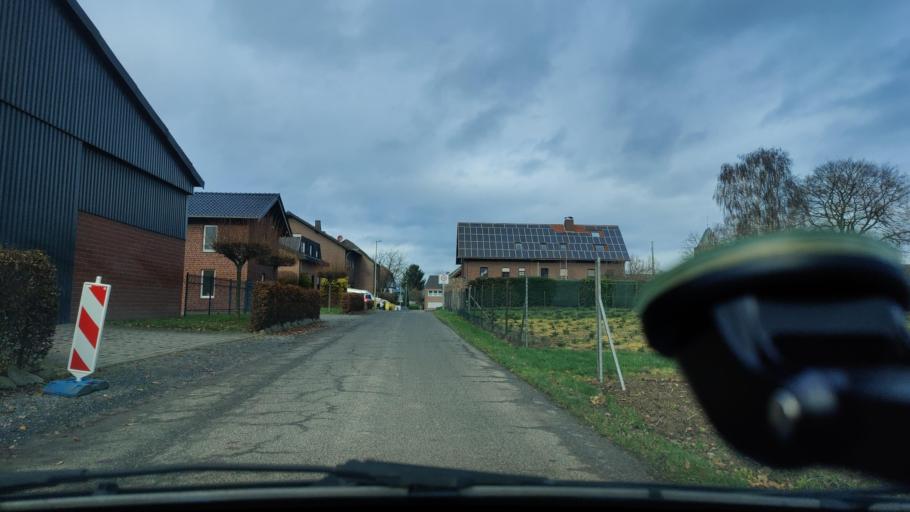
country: DE
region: North Rhine-Westphalia
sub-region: Regierungsbezirk Koln
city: Titz
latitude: 51.0069
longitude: 6.3865
